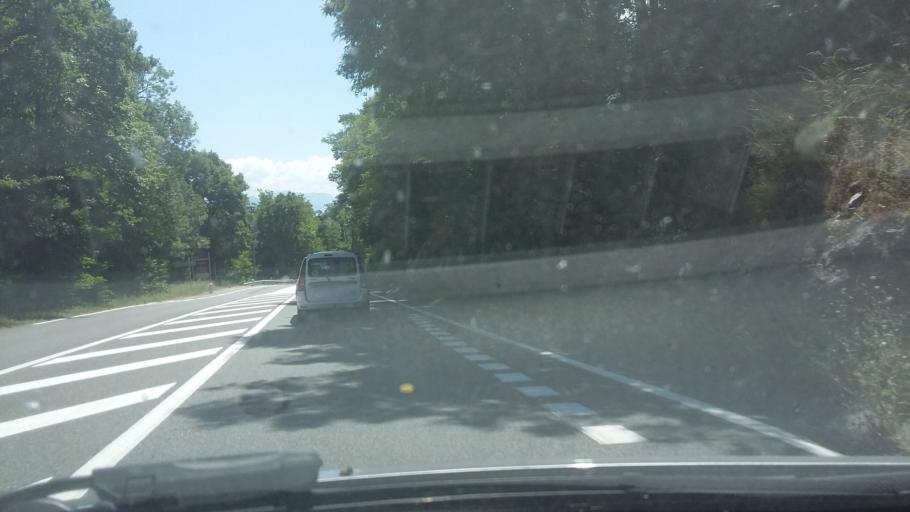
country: FR
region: Rhone-Alpes
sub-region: Departement de la Savoie
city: Le Bourget-du-Lac
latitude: 45.6698
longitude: 5.8549
